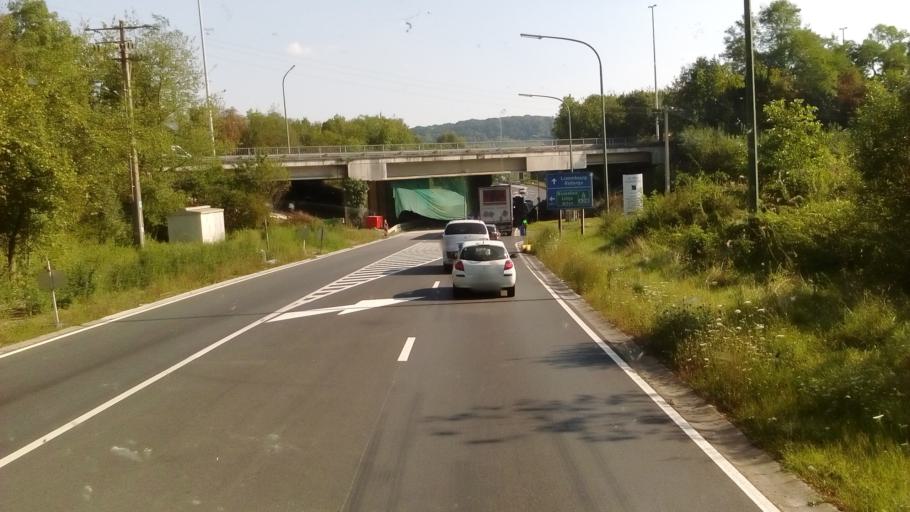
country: BE
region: Wallonia
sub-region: Province du Luxembourg
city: Aubange
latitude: 49.5543
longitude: 5.8088
